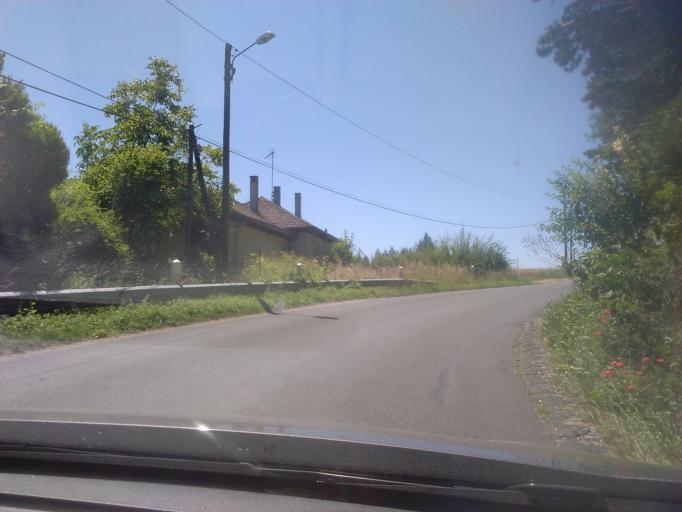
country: FR
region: Centre
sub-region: Departement du Loir-et-Cher
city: Saint-Sulpice-de-Pommeray
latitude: 47.6086
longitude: 1.2353
